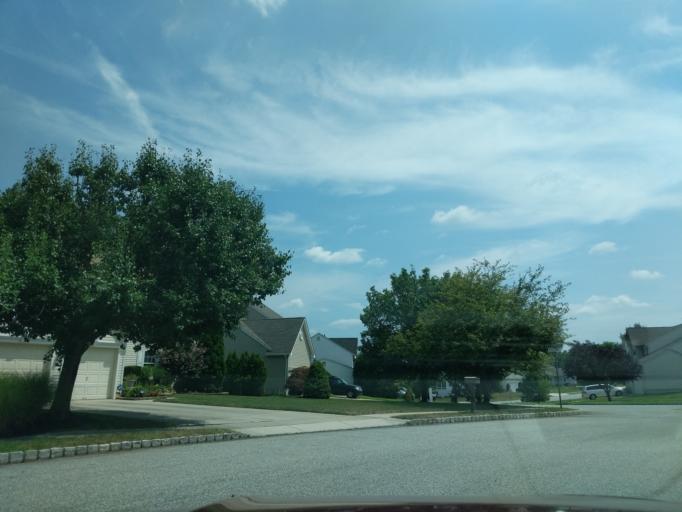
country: US
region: New Jersey
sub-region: Gloucester County
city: Woodbury
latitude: 39.8346
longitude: -75.1162
